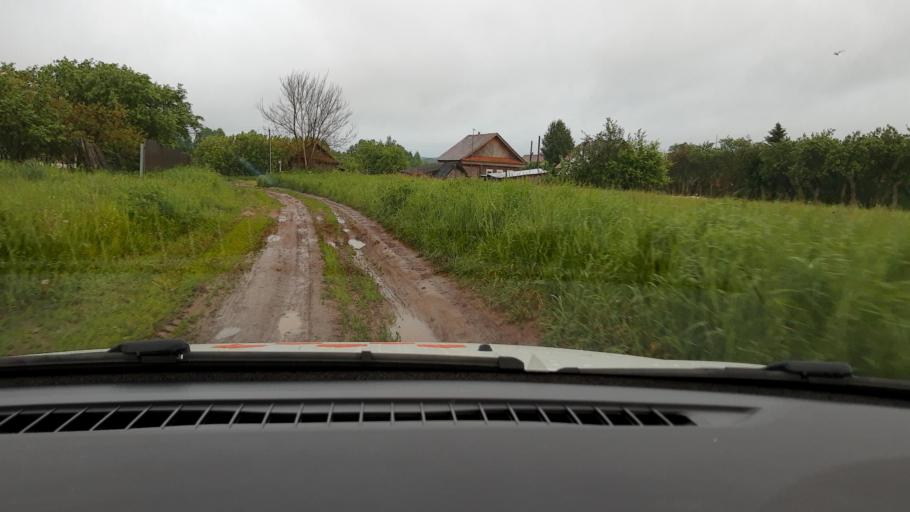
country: RU
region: Nizjnij Novgorod
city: Novaya Balakhna
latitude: 56.6331
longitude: 43.6229
